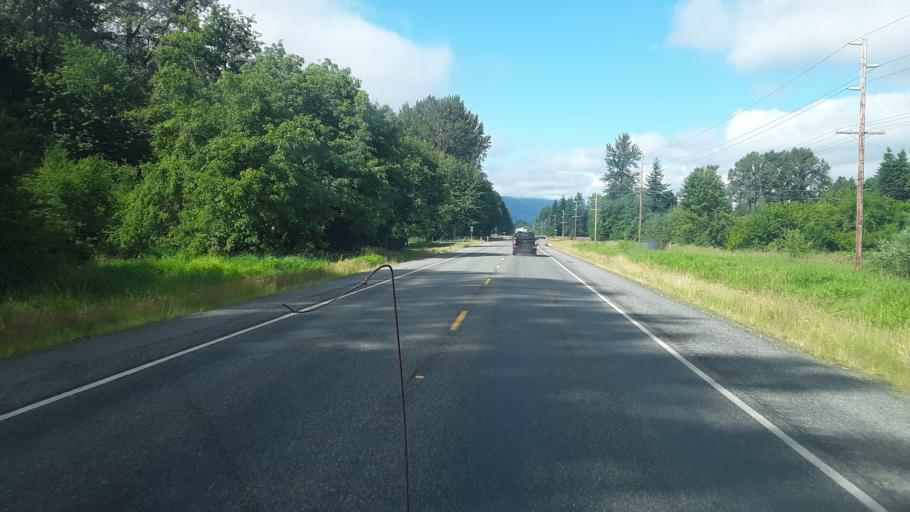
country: US
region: Washington
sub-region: Lewis County
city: Morton
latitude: 46.5601
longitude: -121.7213
